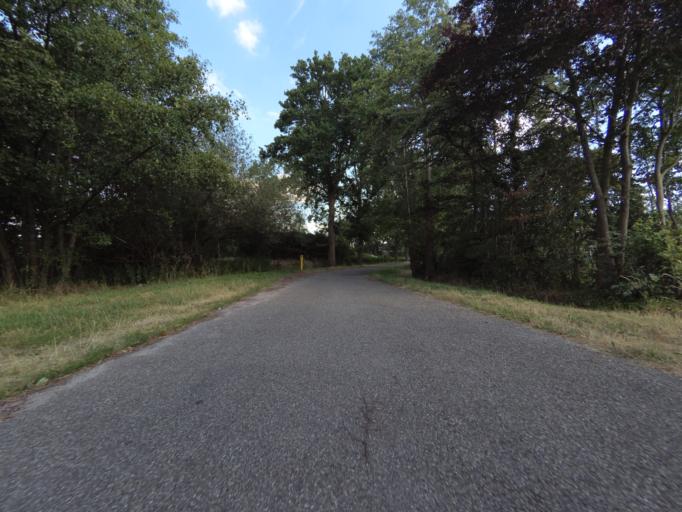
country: NL
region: Overijssel
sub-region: Gemeente Oldenzaal
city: Oldenzaal
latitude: 52.3303
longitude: 6.9167
